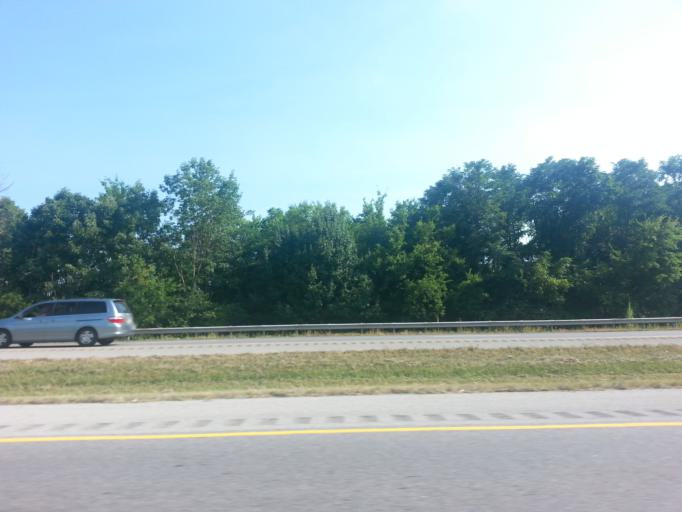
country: US
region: Tennessee
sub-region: Blount County
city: Maryville
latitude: 35.7563
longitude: -84.0325
